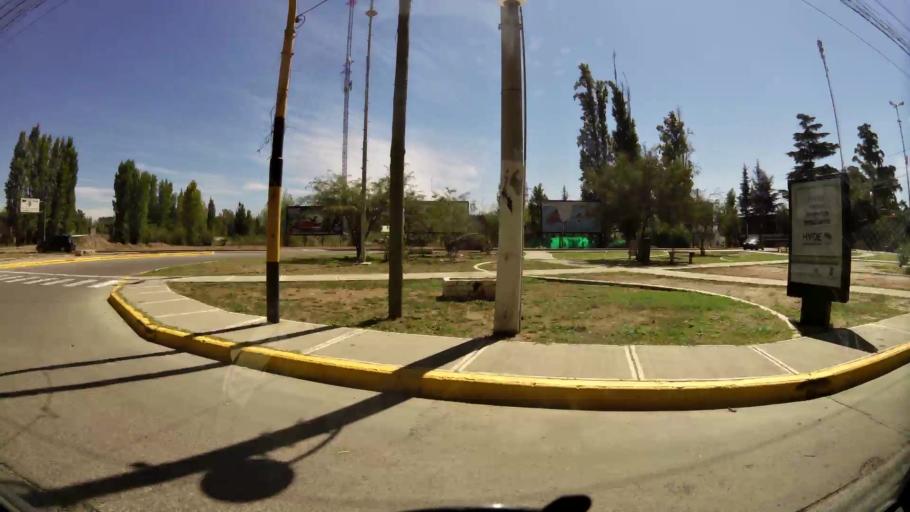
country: AR
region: Mendoza
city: Lujan de Cuyo
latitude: -32.9819
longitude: -68.8597
